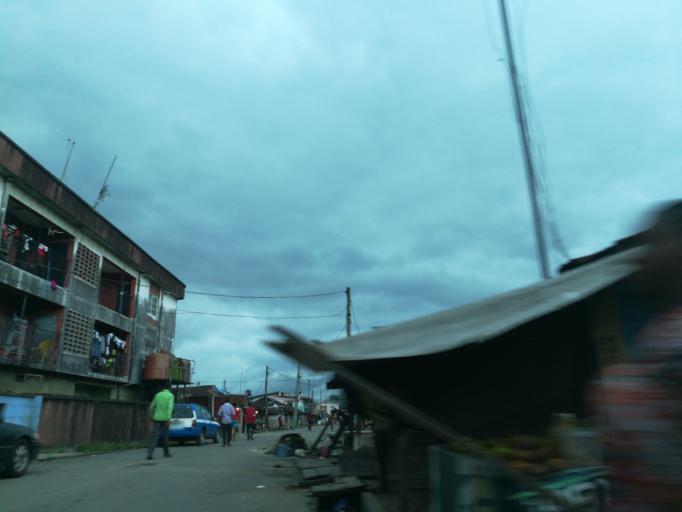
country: NG
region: Rivers
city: Port Harcourt
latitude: 4.7979
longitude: 6.9868
